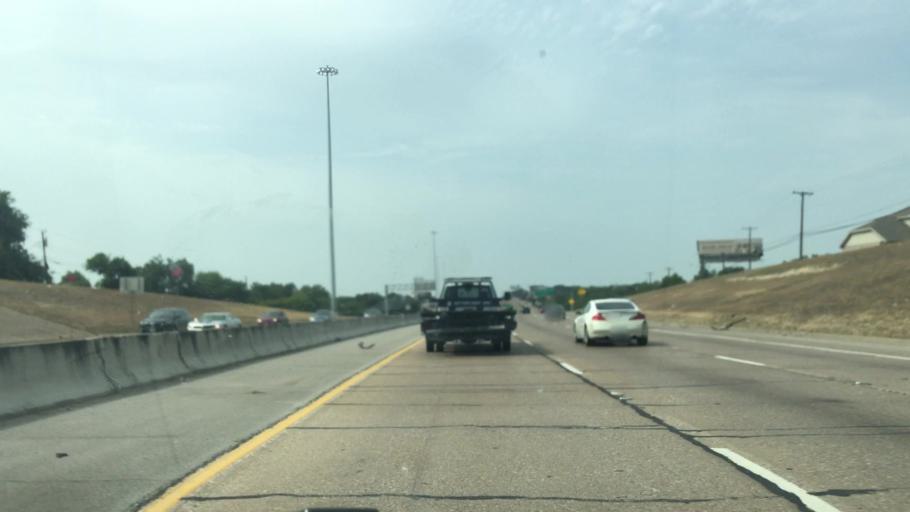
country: US
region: Texas
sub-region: Dallas County
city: DeSoto
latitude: 32.6545
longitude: -96.8232
